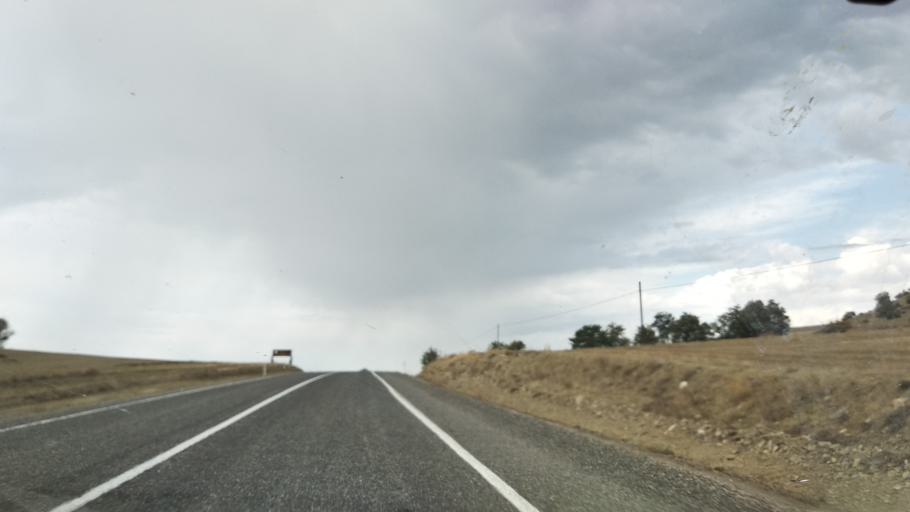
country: TR
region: Bolu
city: Seben
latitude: 40.3327
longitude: 31.4612
